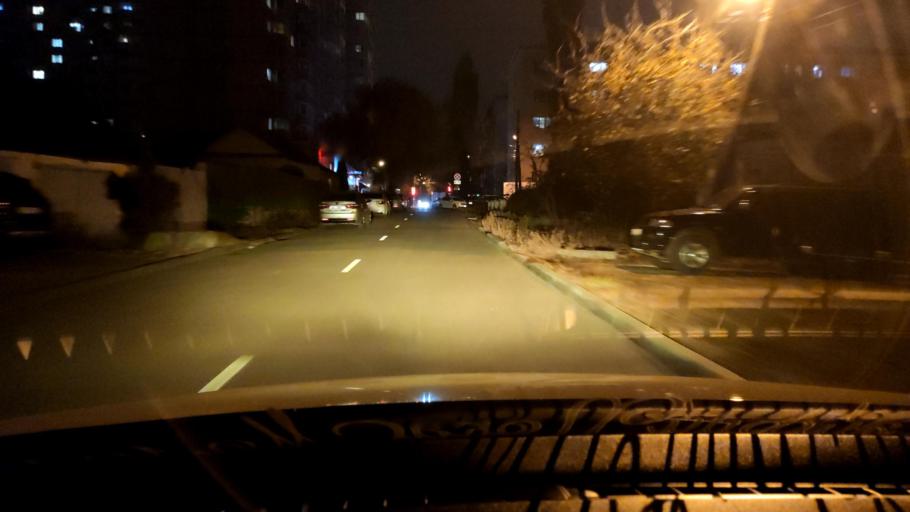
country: RU
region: Voronezj
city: Voronezh
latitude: 51.6721
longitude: 39.1496
